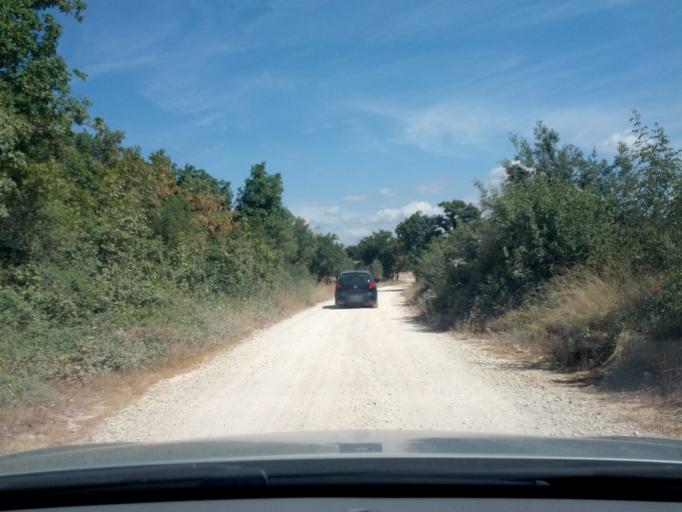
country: HR
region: Istarska
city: Fazana
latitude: 44.9834
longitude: 13.7907
